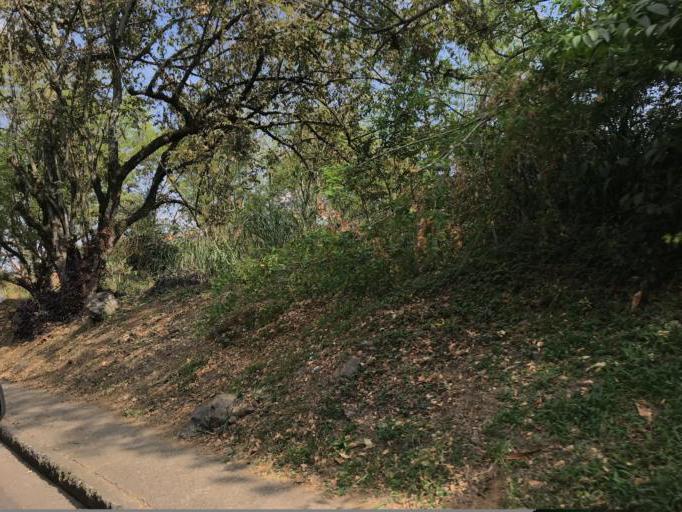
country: CO
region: Valle del Cauca
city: Cali
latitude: 3.4507
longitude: -76.5566
